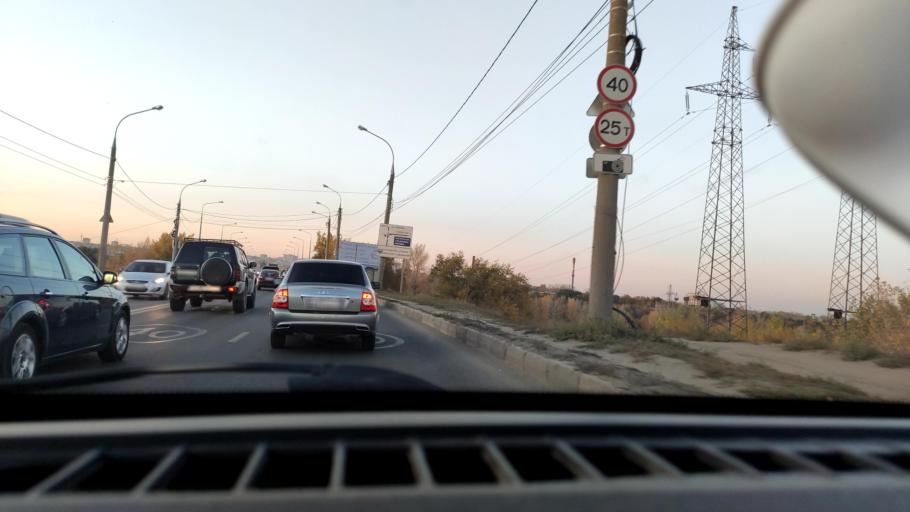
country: RU
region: Samara
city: Samara
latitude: 53.1660
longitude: 50.1969
